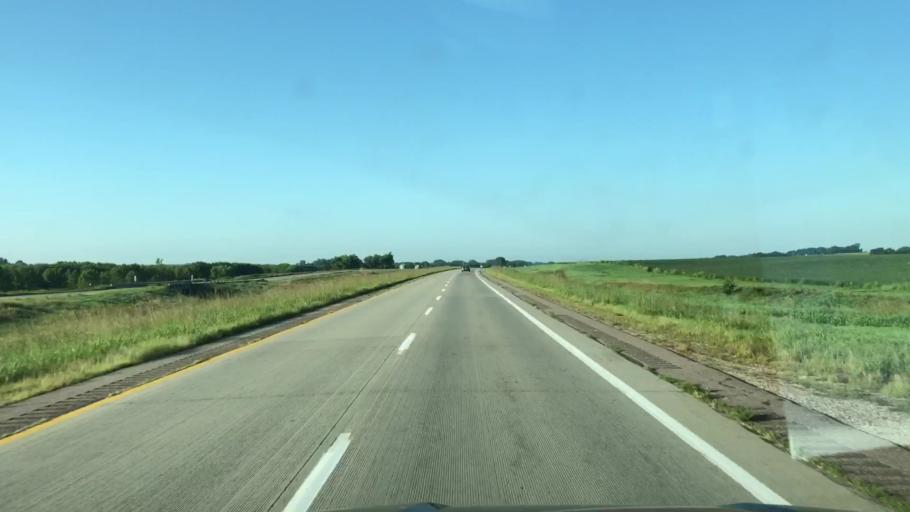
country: US
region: Iowa
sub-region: Plymouth County
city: Le Mars
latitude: 42.8877
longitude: -96.0954
